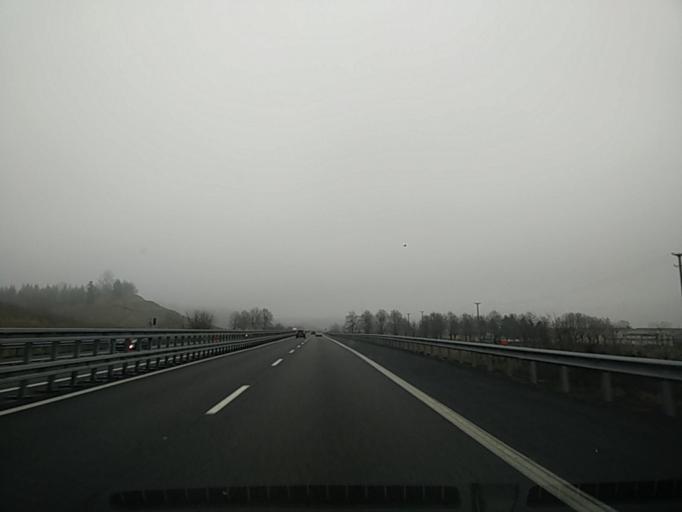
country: IT
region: Piedmont
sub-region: Provincia di Asti
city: Azzano d'Asti
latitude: 44.9082
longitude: 8.2641
